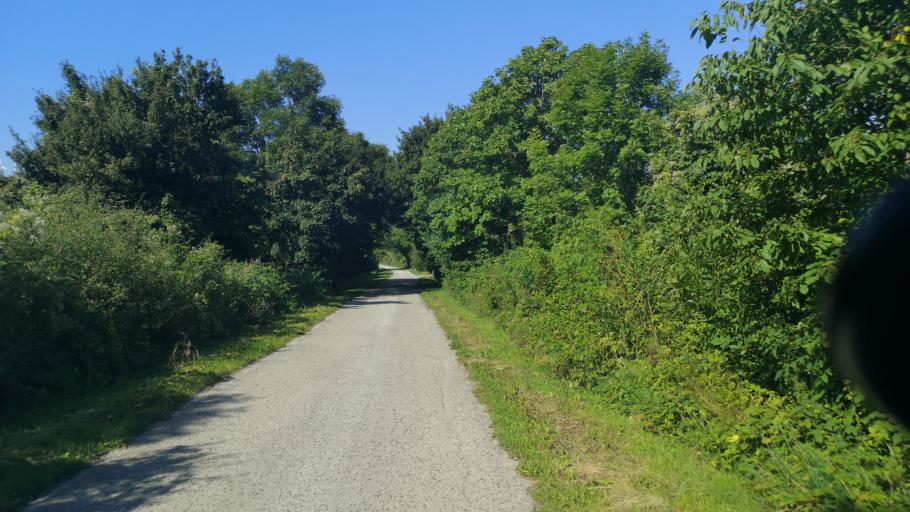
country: SK
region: Trnavsky
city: Smolenice
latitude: 48.5738
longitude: 17.4081
